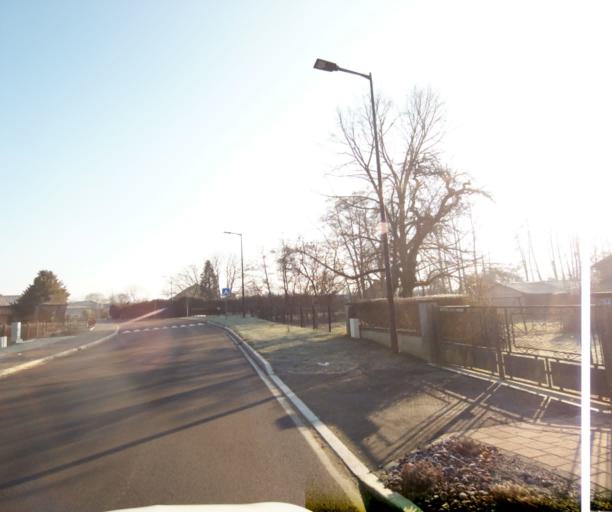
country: FR
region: Champagne-Ardenne
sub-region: Departement de la Haute-Marne
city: Montier-en-Der
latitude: 48.4332
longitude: 4.7219
